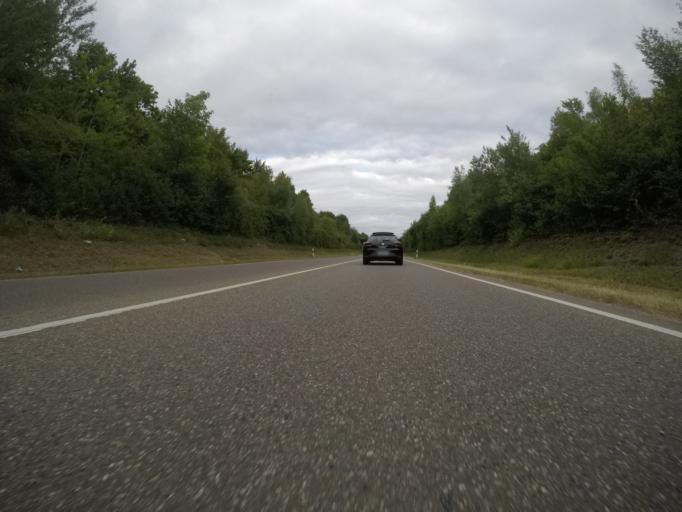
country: DE
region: Baden-Wuerttemberg
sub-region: Regierungsbezirk Stuttgart
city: Korntal
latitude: 48.8081
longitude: 9.1134
